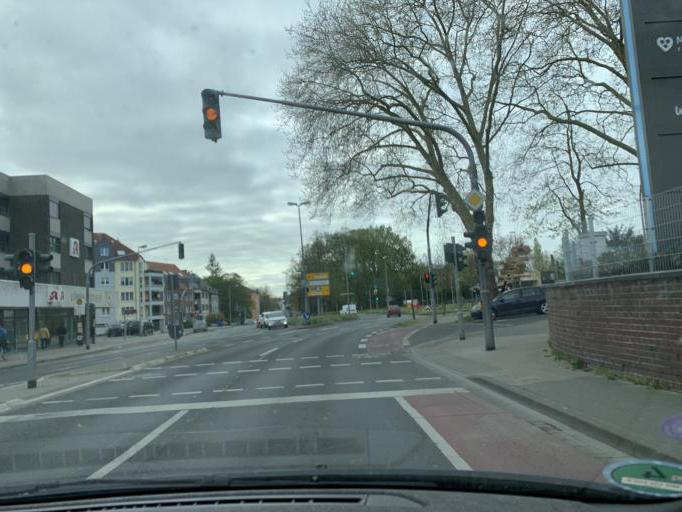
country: DE
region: North Rhine-Westphalia
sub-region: Regierungsbezirk Dusseldorf
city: Monchengladbach
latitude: 51.1540
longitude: 6.4515
